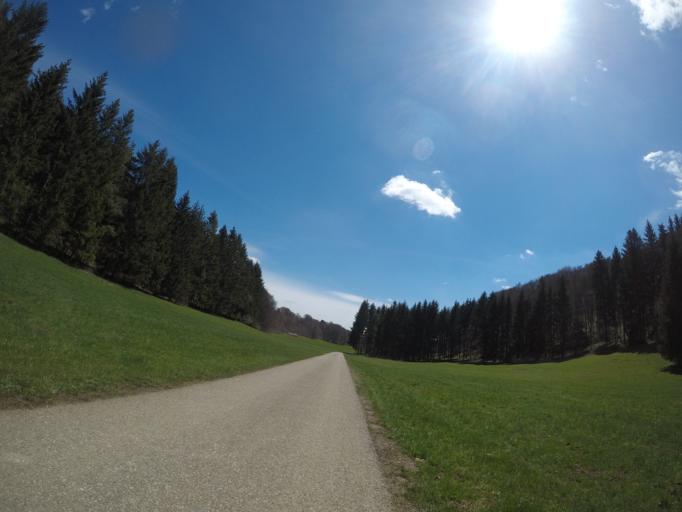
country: DE
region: Baden-Wuerttemberg
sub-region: Tuebingen Region
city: Westerheim
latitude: 48.5121
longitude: 9.5988
